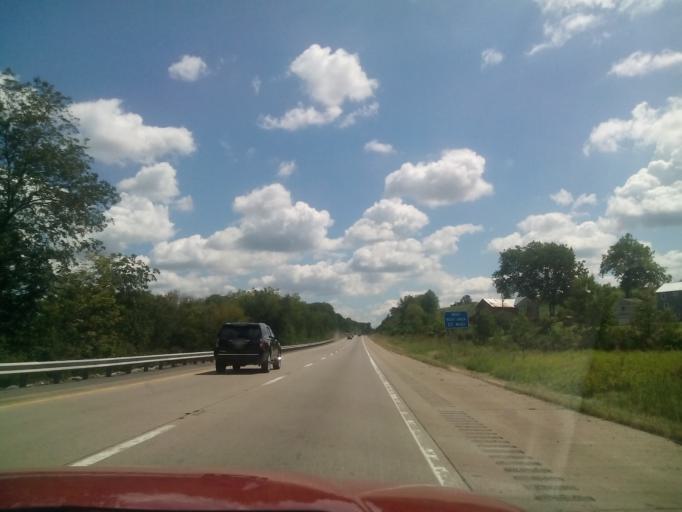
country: US
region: Pennsylvania
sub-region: Northumberland County
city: Milton
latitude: 41.0046
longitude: -76.7604
